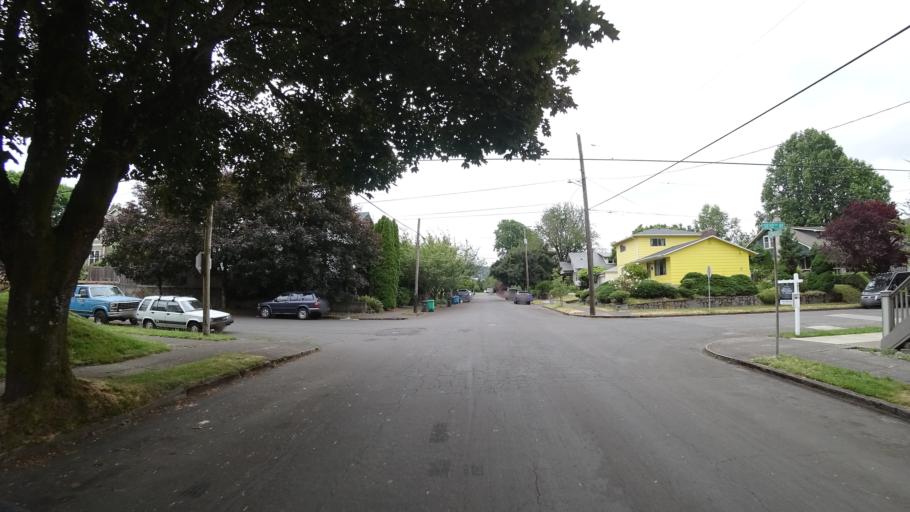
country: US
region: Oregon
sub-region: Multnomah County
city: Portland
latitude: 45.4921
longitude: -122.6530
